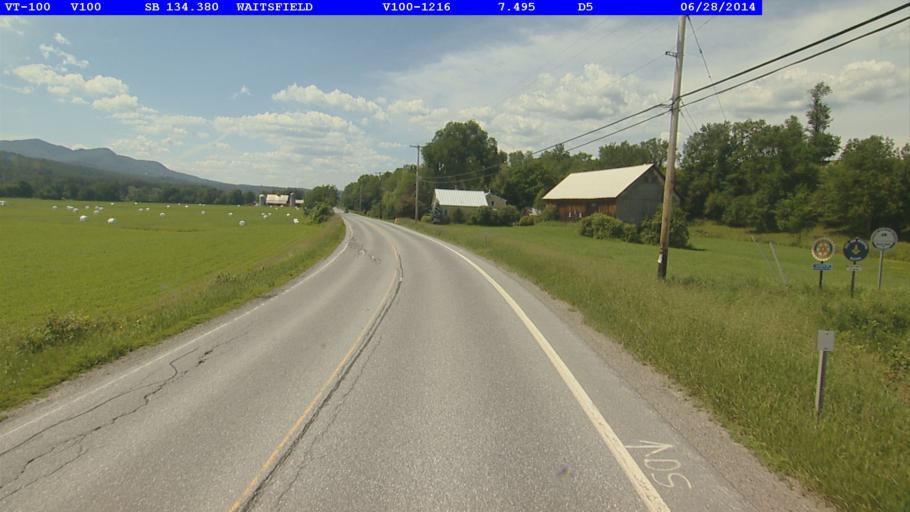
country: US
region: Vermont
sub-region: Washington County
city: Waterbury
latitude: 44.2341
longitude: -72.7813
